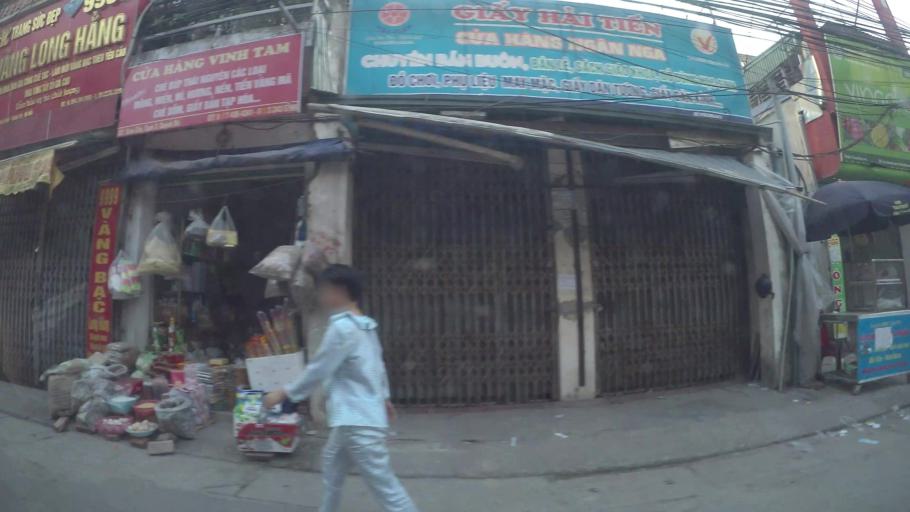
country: VN
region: Ha Noi
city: Van Dien
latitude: 20.9349
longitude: 105.8371
